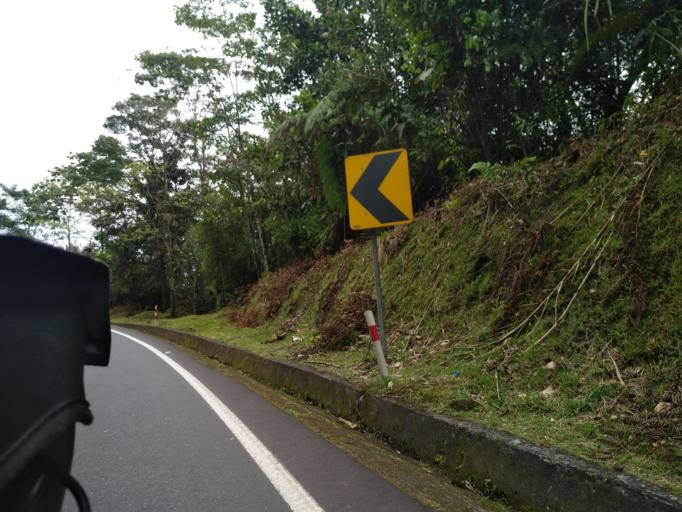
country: EC
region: Pastaza
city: Puyo
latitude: -1.4714
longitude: -78.1011
